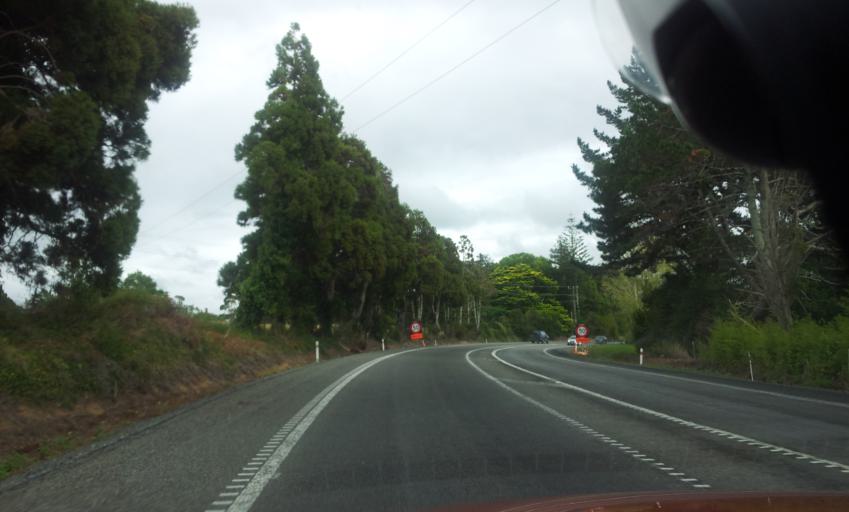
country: NZ
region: Auckland
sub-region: Auckland
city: Wellsford
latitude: -36.3151
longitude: 174.5361
